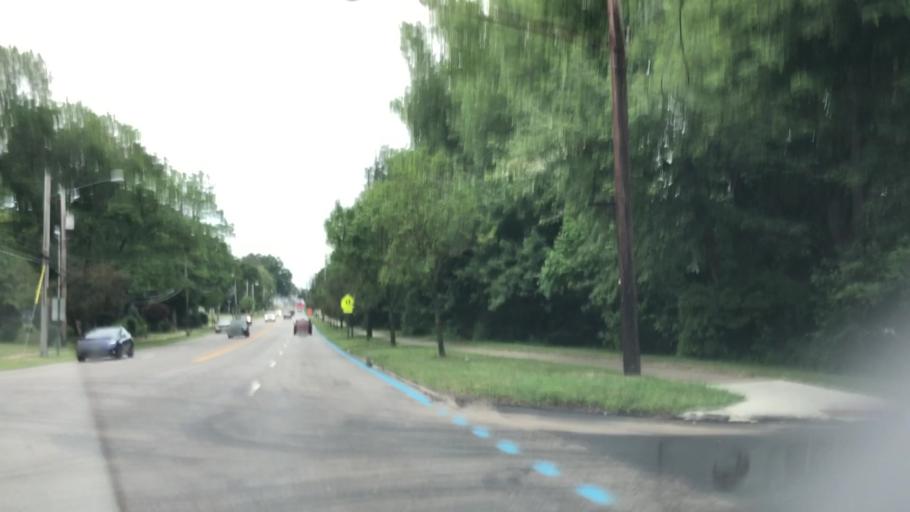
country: US
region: Ohio
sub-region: Summit County
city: Sawyerwood
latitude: 41.0539
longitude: -81.4390
